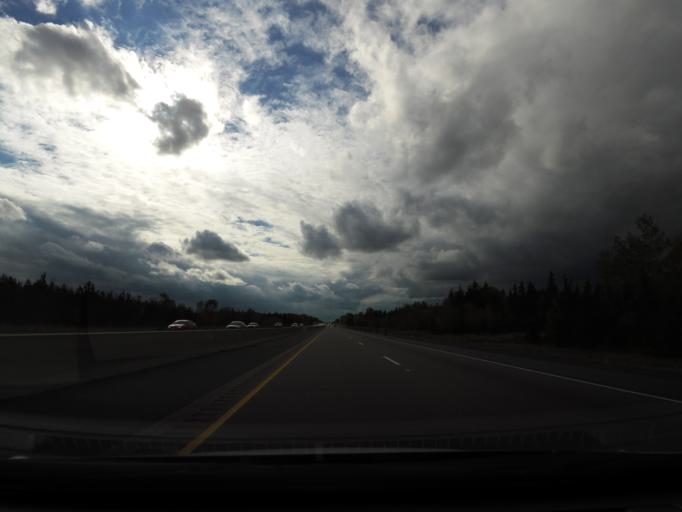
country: CA
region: Ontario
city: Belleville
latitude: 44.2153
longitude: -77.3187
